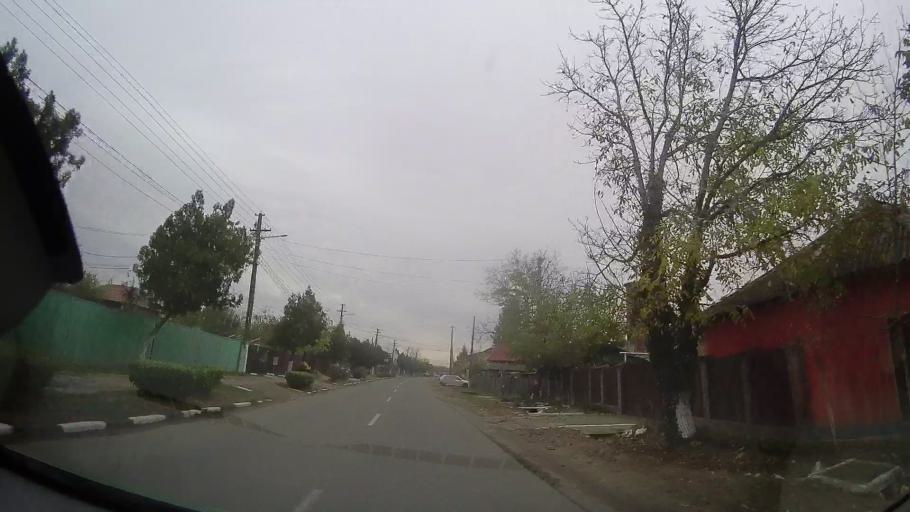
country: RO
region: Prahova
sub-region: Comuna Ceptura
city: Ceptura de Jos
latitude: 45.0153
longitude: 26.3305
